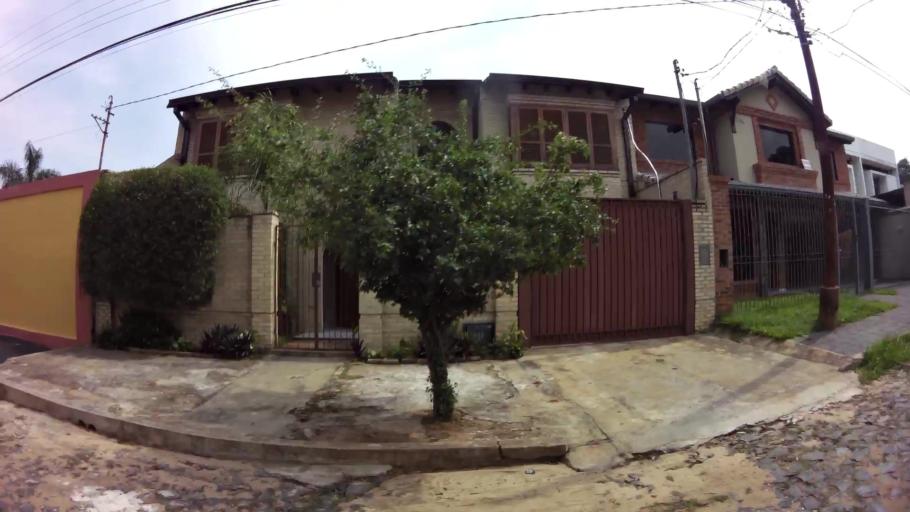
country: PY
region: Central
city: Fernando de la Mora
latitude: -25.2719
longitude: -57.5580
